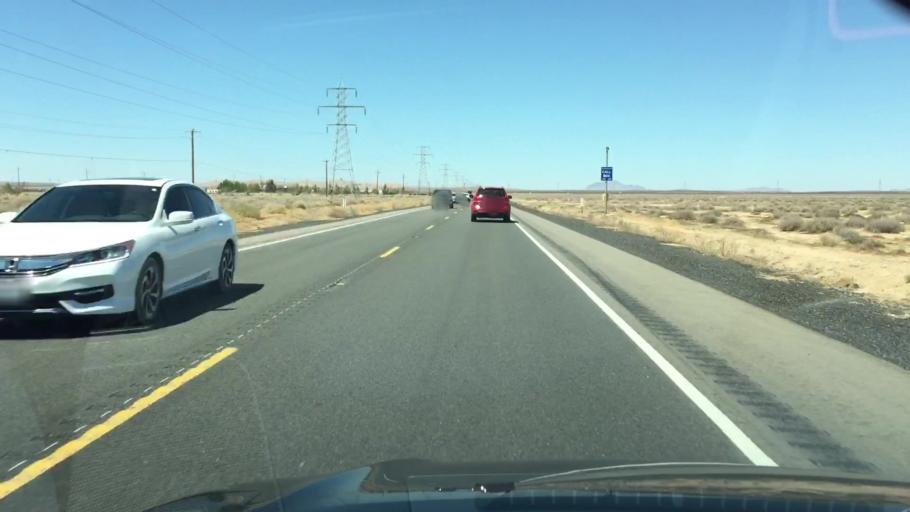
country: US
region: California
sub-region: Kern County
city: Boron
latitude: 35.0066
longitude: -117.5455
